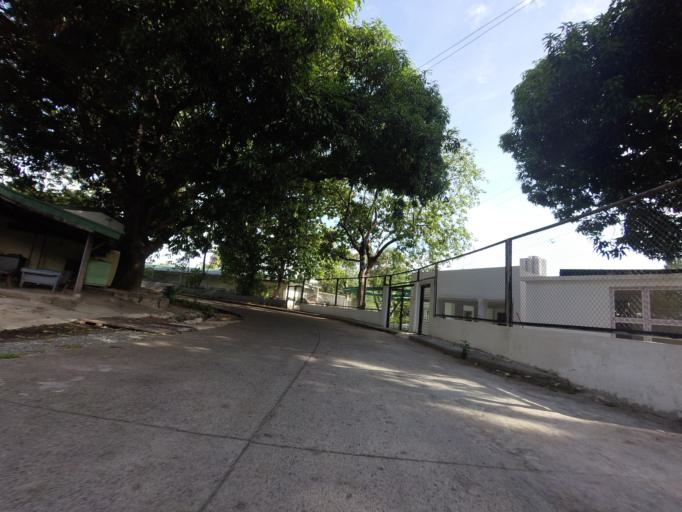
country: PH
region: Metro Manila
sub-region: Mandaluyong
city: Mandaluyong City
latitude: 14.5798
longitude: 121.0390
